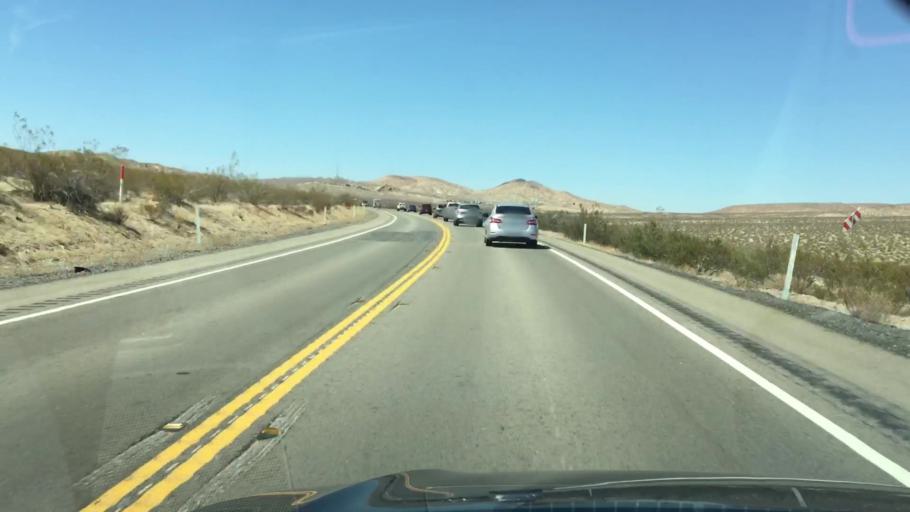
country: US
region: California
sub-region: Kern County
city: Ridgecrest
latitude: 35.3213
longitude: -117.6096
